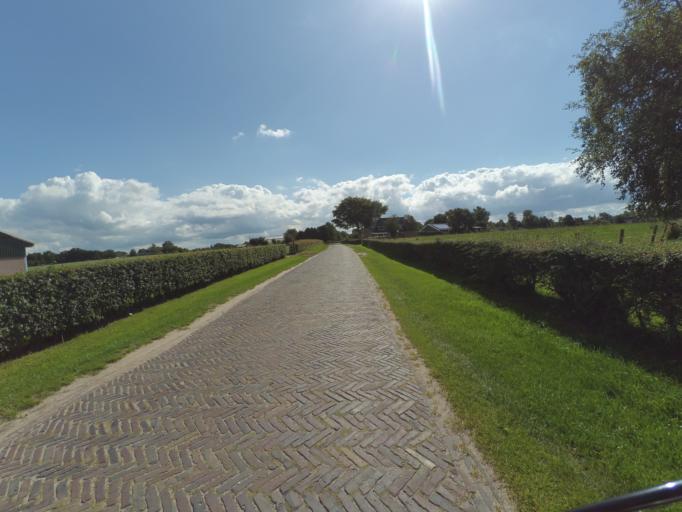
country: NL
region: Friesland
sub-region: Gemeente Achtkarspelen
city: Twijzelerheide
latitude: 53.2167
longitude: 6.0515
